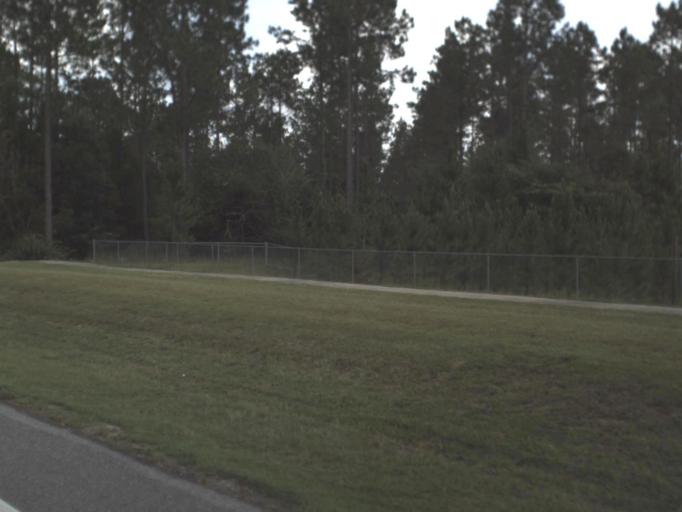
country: US
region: Florida
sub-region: Madison County
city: Madison
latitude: 30.4244
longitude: -83.3073
